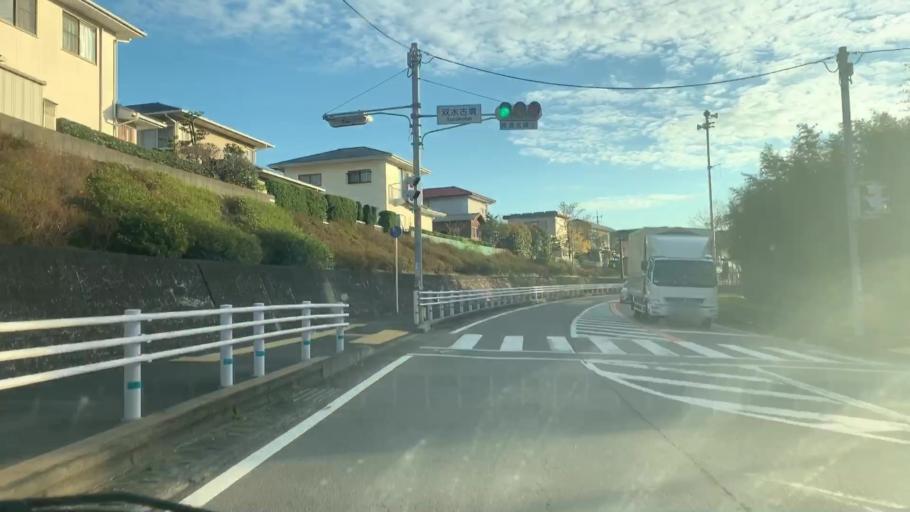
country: JP
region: Saga Prefecture
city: Karatsu
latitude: 33.3982
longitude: 129.9877
